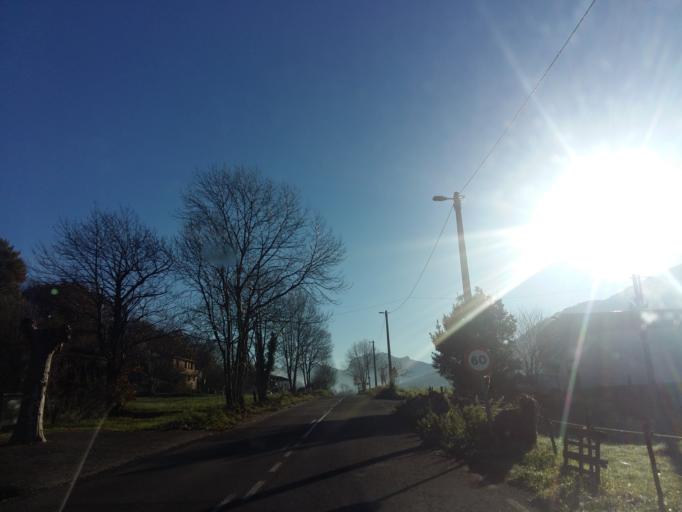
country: ES
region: Cantabria
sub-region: Provincia de Cantabria
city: Ramales de la Victoria
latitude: 43.2766
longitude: -3.5217
